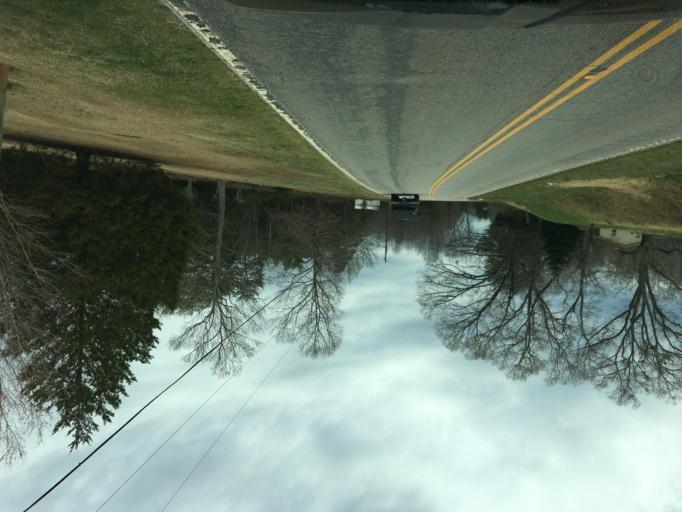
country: US
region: South Carolina
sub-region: Greenville County
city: Golden Grove
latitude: 34.6994
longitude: -82.4171
